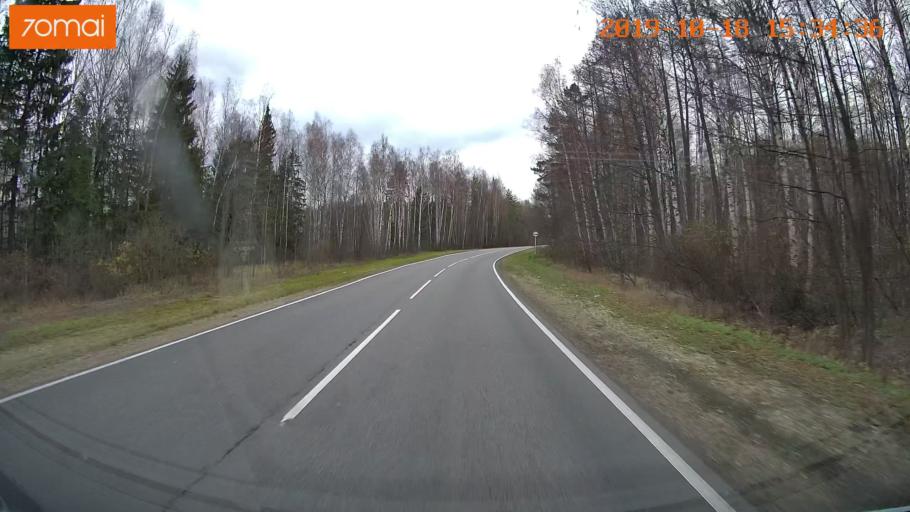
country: RU
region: Vladimir
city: Anopino
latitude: 55.8561
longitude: 40.6401
